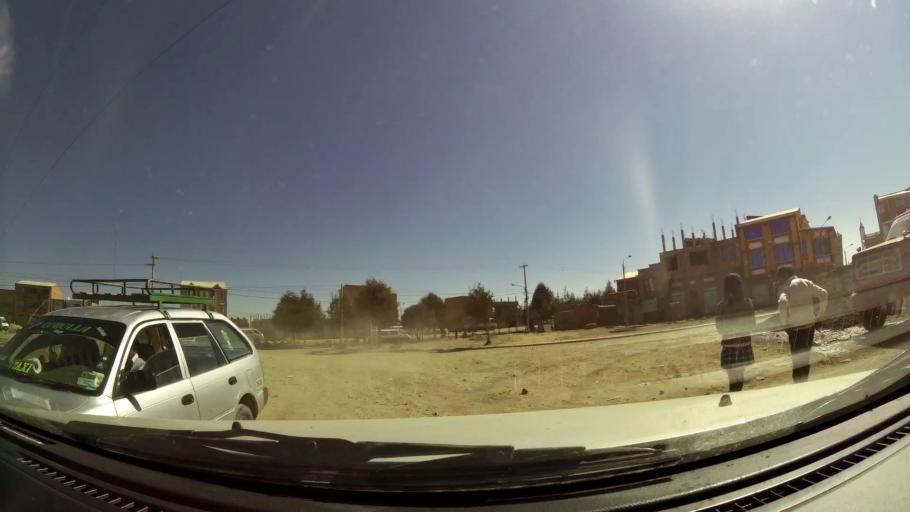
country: BO
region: La Paz
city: La Paz
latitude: -16.5705
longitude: -68.2230
